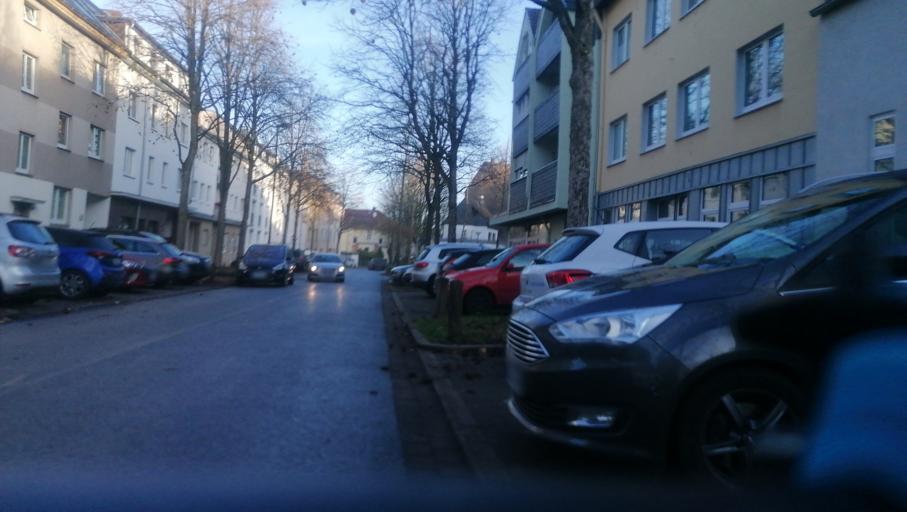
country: DE
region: North Rhine-Westphalia
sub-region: Regierungsbezirk Arnsberg
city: Dortmund
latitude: 51.4861
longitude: 7.4985
